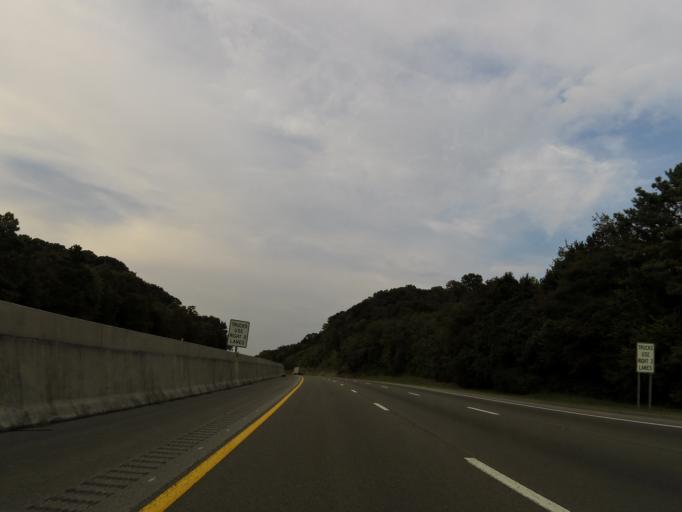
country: US
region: Tennessee
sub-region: Davidson County
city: Belle Meade
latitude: 36.0903
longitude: -86.9401
